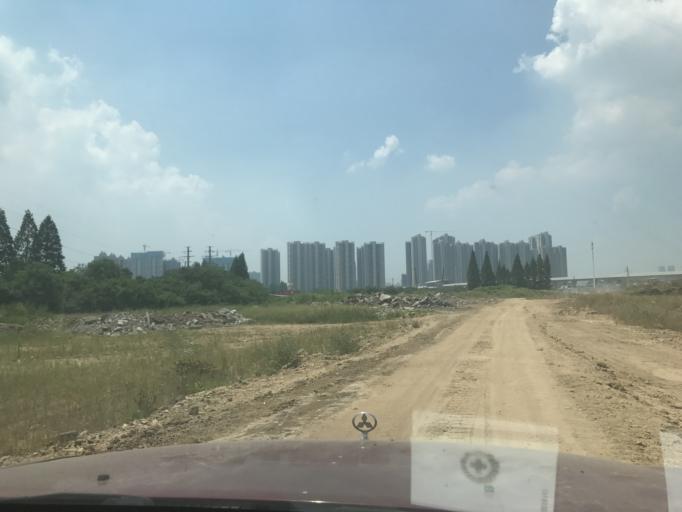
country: CN
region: Hubei
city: Zhanjiaji
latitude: 30.6835
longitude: 114.3406
